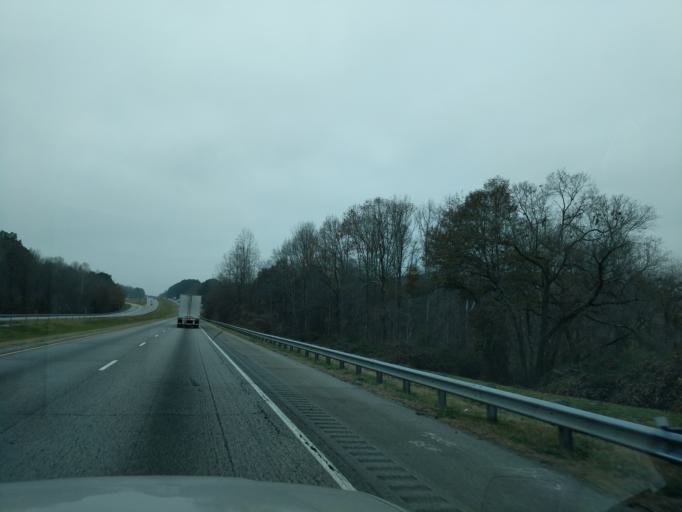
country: US
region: Georgia
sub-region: Franklin County
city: Lavonia
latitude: 34.4333
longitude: -83.1480
